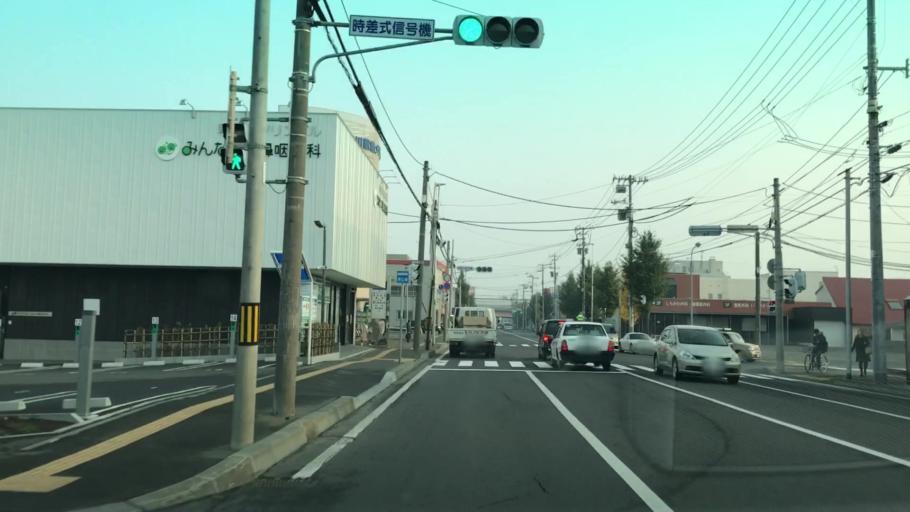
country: JP
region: Hokkaido
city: Sapporo
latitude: 43.0984
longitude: 141.3252
